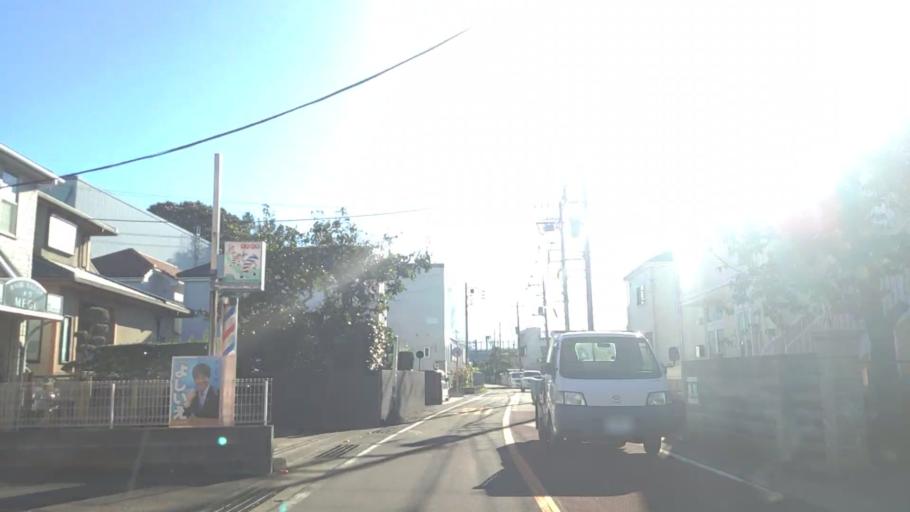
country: JP
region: Kanagawa
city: Atsugi
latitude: 35.4249
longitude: 139.3687
